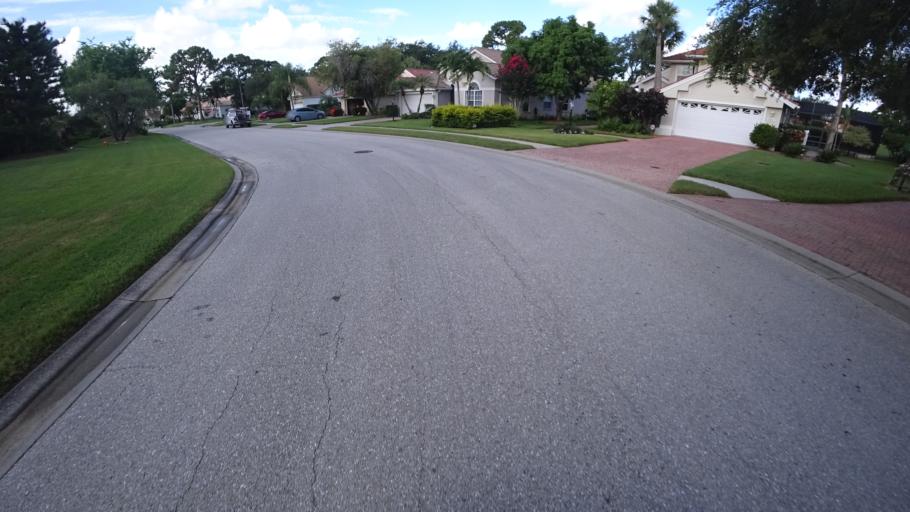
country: US
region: Florida
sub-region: Sarasota County
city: Desoto Lakes
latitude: 27.4105
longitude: -82.4871
